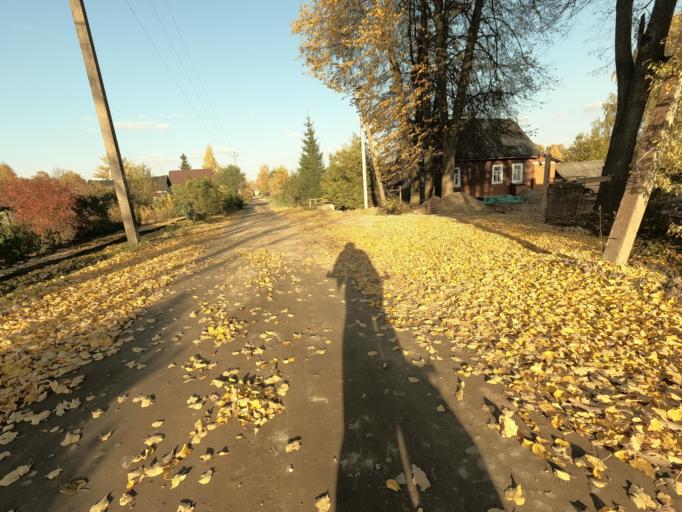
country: RU
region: Leningrad
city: Mga
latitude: 59.7516
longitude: 31.0557
